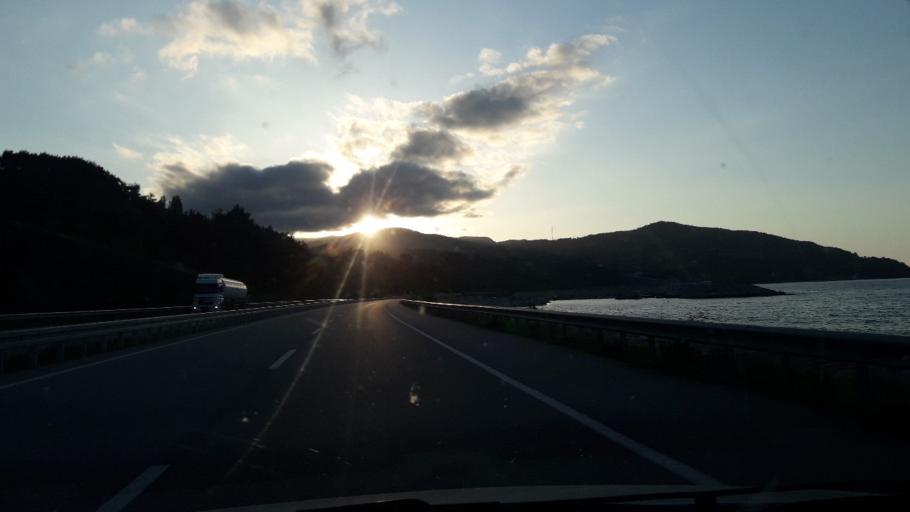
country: TR
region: Sinop
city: Dikmen
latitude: 41.7137
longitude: 35.2818
